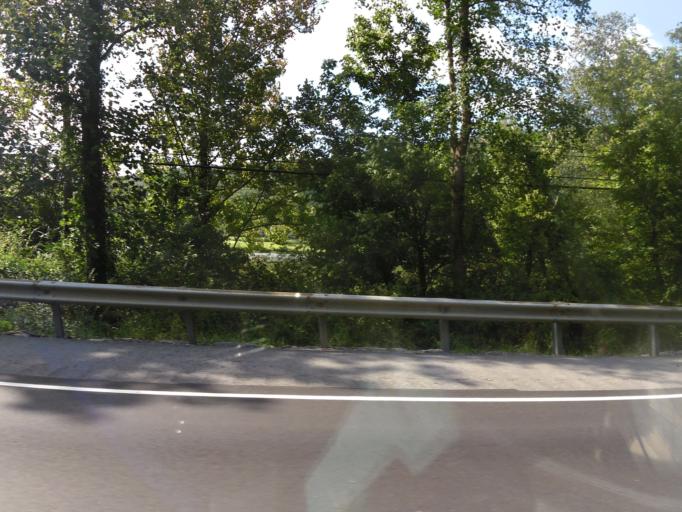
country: US
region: Kentucky
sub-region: Bell County
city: Pineville
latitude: 36.7411
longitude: -83.6944
